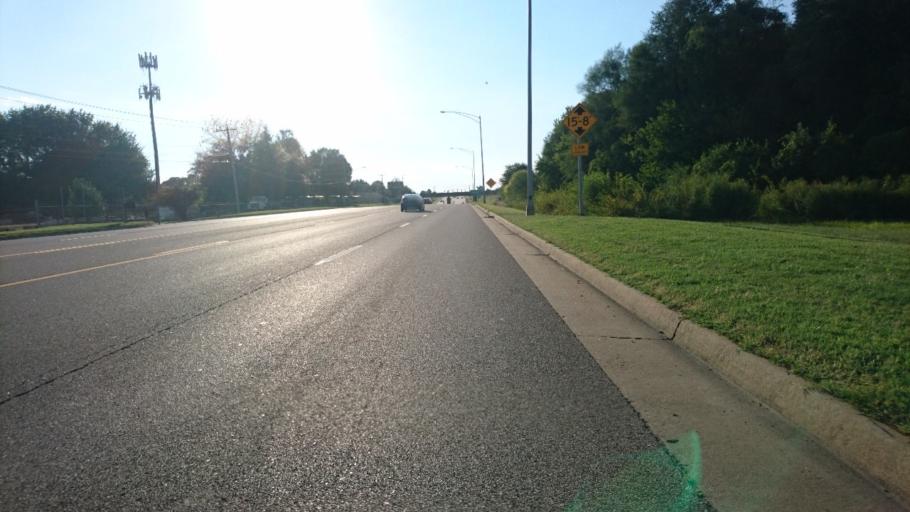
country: US
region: Missouri
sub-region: Greene County
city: Springfield
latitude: 37.2126
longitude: -93.3751
